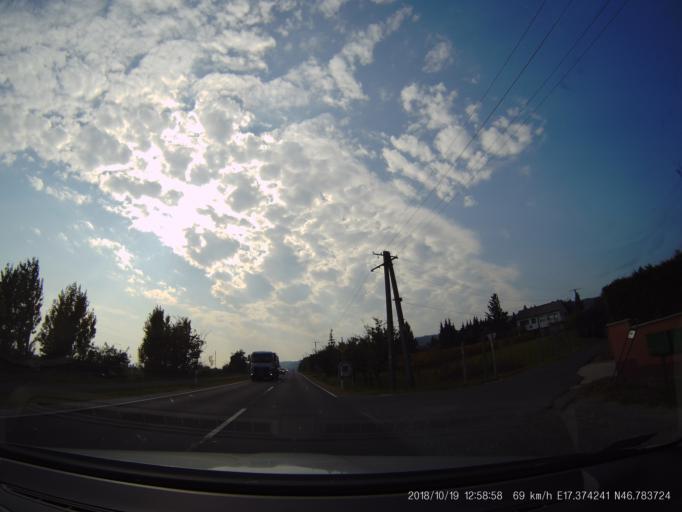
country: HU
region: Zala
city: Vonyarcvashegy
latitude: 46.7837
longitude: 17.3742
